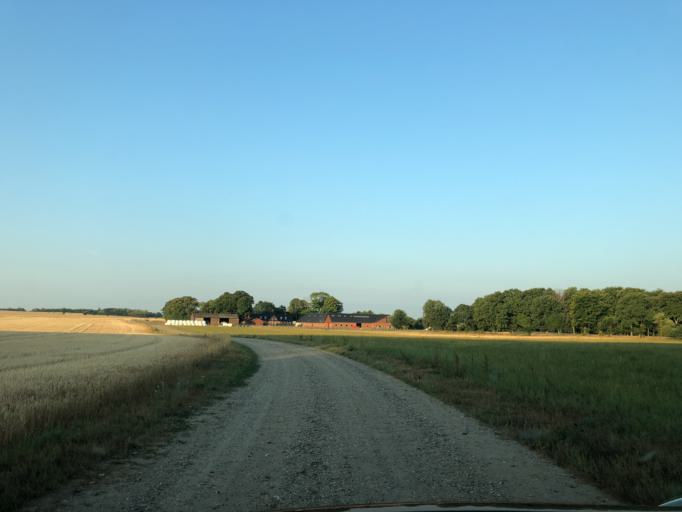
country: DK
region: Central Jutland
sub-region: Skanderborg Kommune
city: Skanderborg
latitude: 56.0914
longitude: 9.8728
